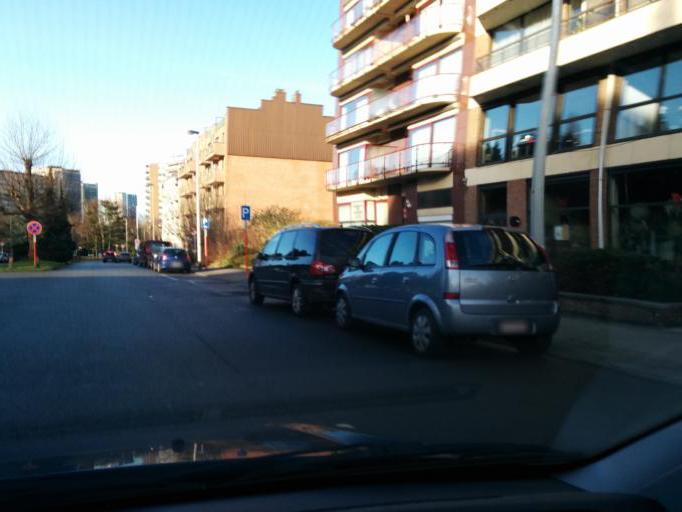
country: BE
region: Flanders
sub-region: Provincie Vlaams-Brabant
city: Wemmel
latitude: 50.8734
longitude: 4.3116
